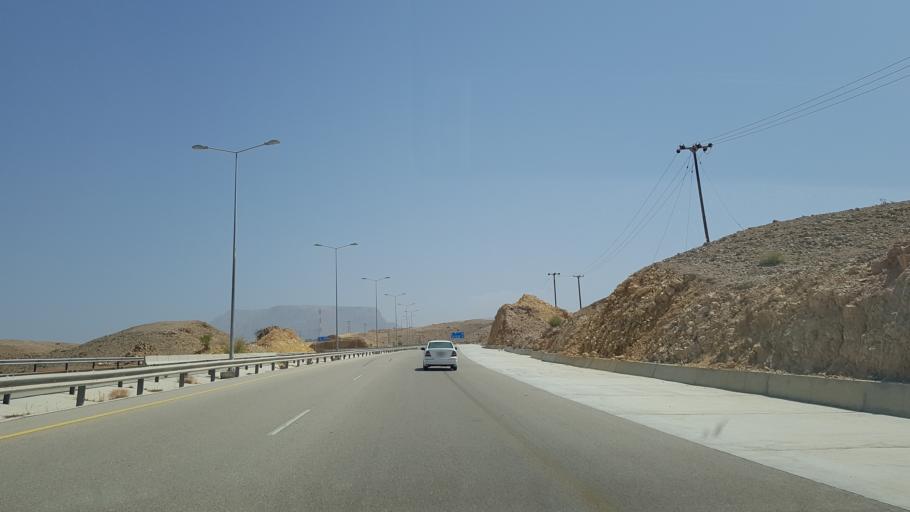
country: OM
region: Ash Sharqiyah
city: Al Qabil
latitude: 23.1151
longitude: 58.9780
